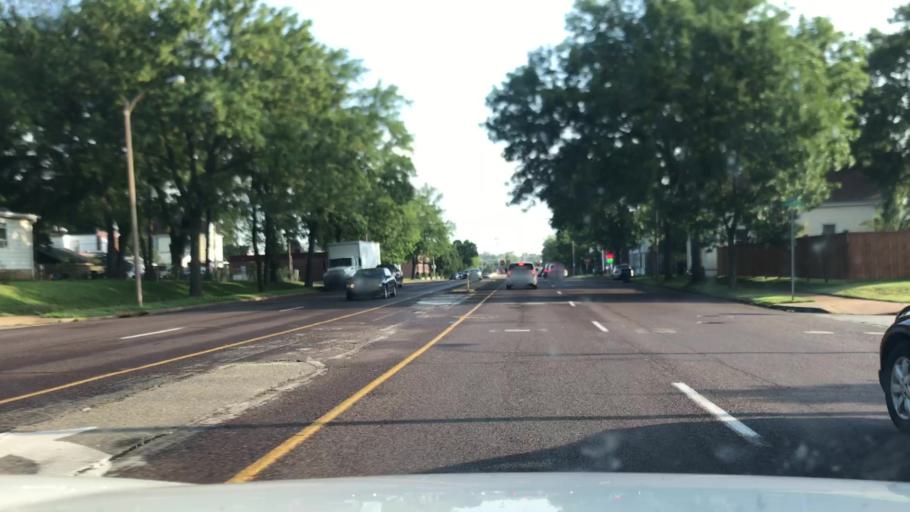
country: US
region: Missouri
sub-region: Saint Louis County
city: Maplewood
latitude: 38.6024
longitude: -90.3078
